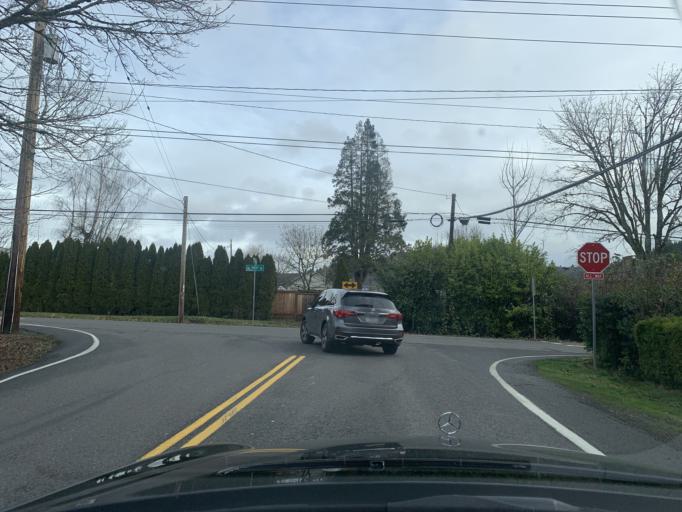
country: US
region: Oregon
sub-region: Multnomah County
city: Gresham
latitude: 45.4674
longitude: -122.4670
